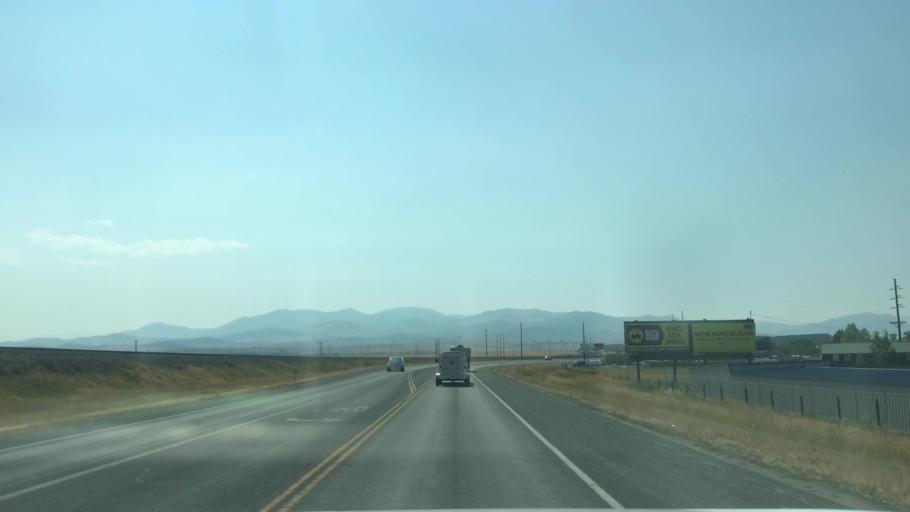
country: US
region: Montana
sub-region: Lewis and Clark County
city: East Helena
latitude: 46.5868
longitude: -111.8940
